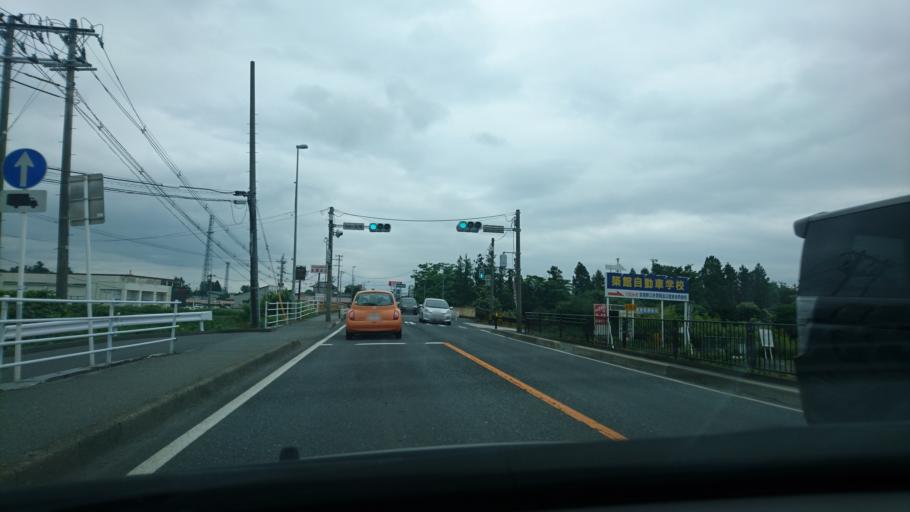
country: JP
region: Miyagi
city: Furukawa
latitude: 38.7417
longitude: 141.0177
